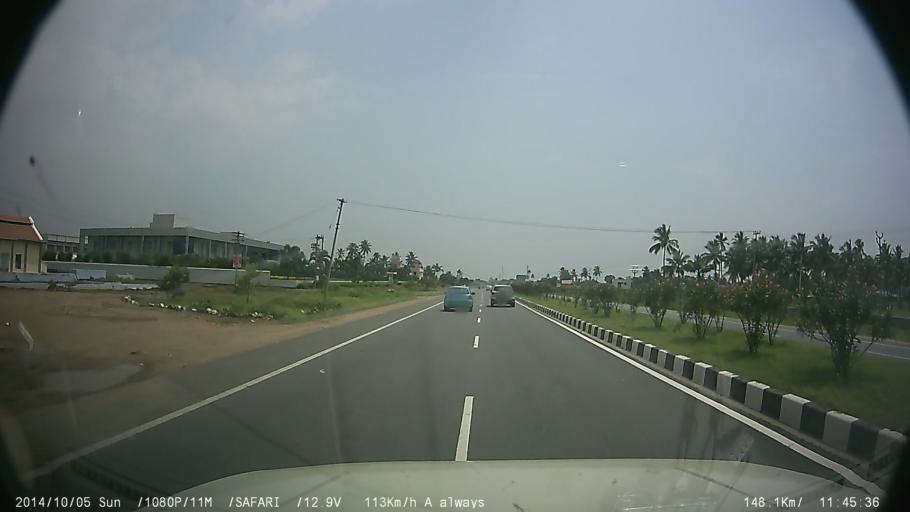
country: IN
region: Tamil Nadu
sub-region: Salem
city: Attur
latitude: 11.5919
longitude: 78.6567
